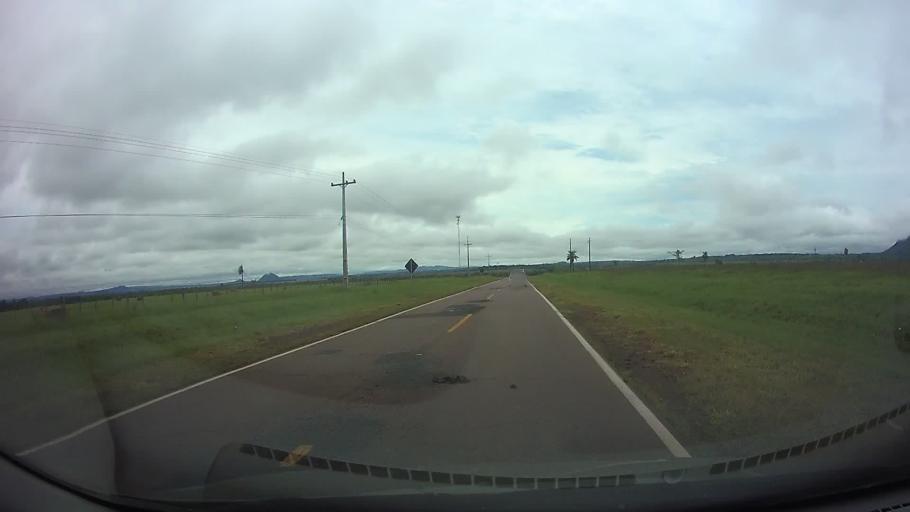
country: PY
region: Paraguari
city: Carapegua
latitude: -25.8261
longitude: -57.1631
